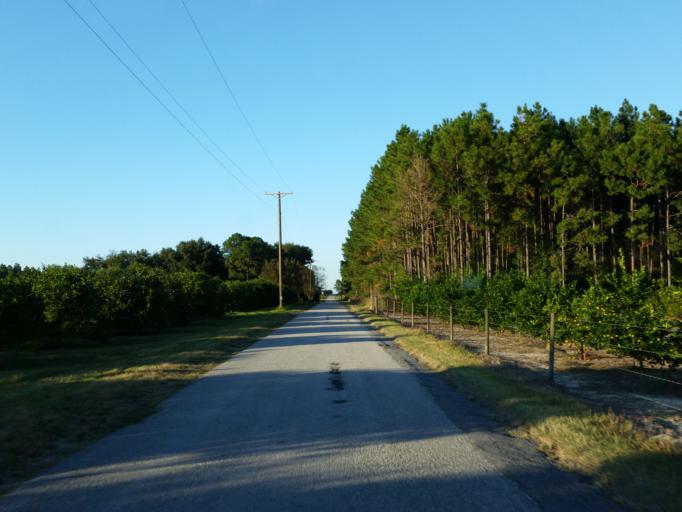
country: US
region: Florida
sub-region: Pasco County
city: Dade City North
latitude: 28.4211
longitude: -82.2616
